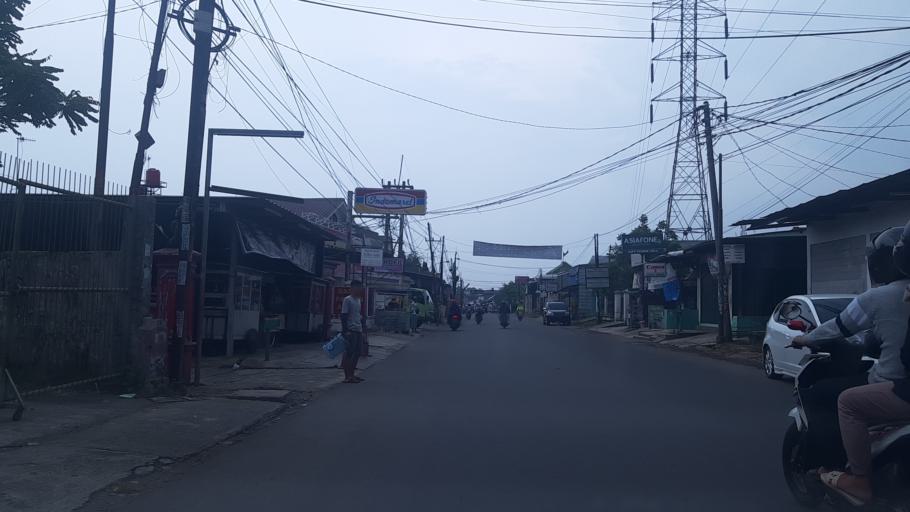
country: ID
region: West Java
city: Cibinong
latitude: -6.5233
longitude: 106.8585
